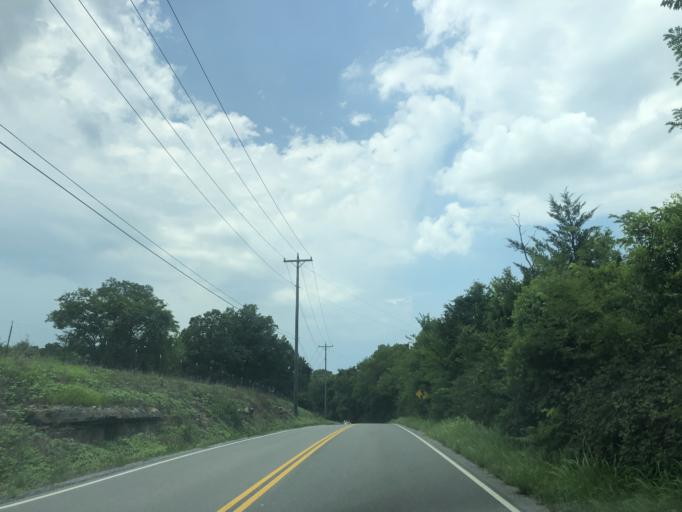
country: US
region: Tennessee
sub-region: Rutherford County
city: La Vergne
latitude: 36.1167
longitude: -86.6517
